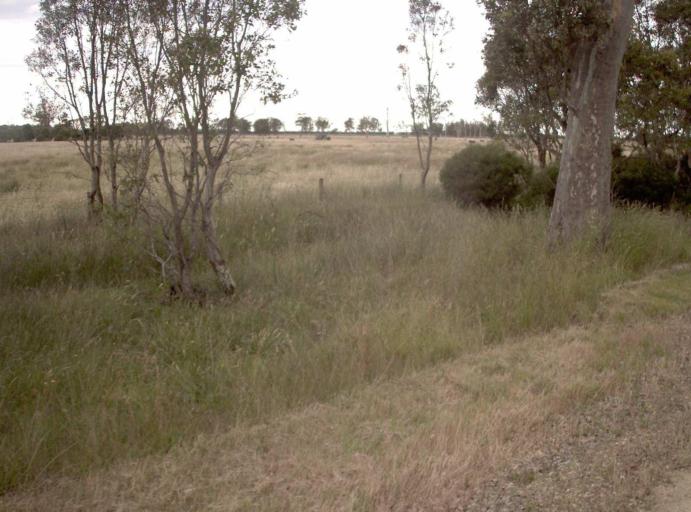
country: AU
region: Victoria
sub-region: Wellington
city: Sale
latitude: -37.9908
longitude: 147.1957
